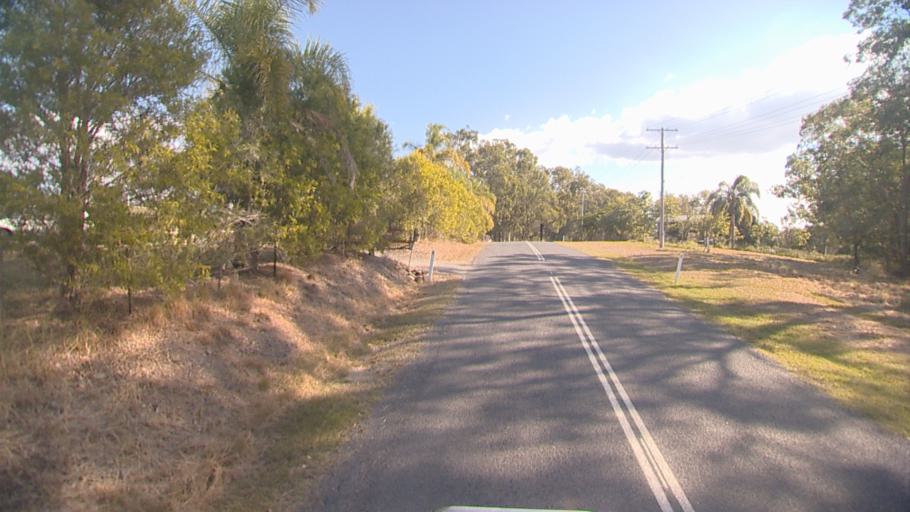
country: AU
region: Queensland
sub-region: Logan
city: Windaroo
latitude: -27.7390
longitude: 153.1609
